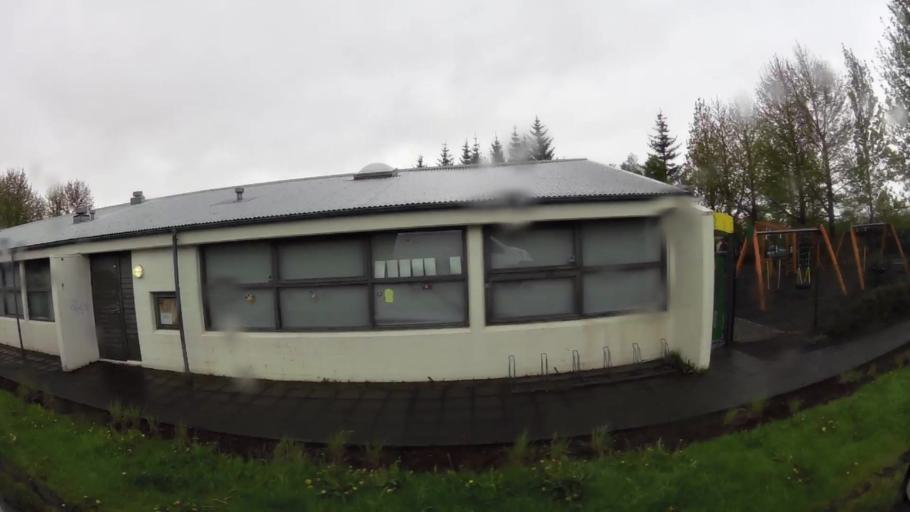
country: IS
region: Capital Region
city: Reykjavik
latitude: 64.0979
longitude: -21.8385
